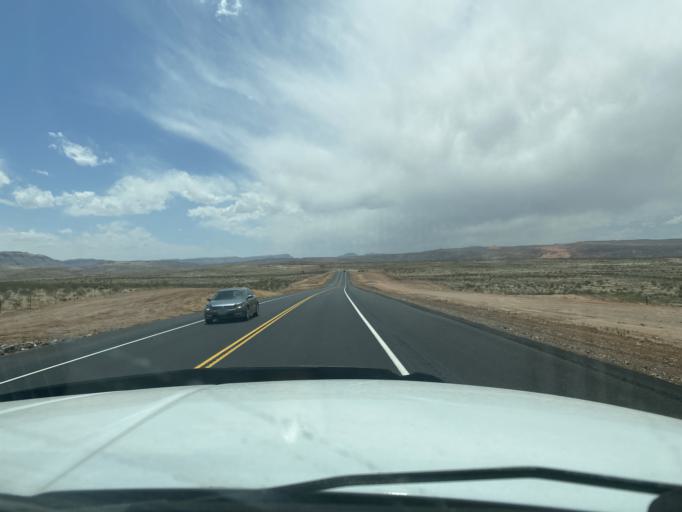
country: US
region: Utah
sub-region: Washington County
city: Hurricane
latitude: 37.1467
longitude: -113.3461
